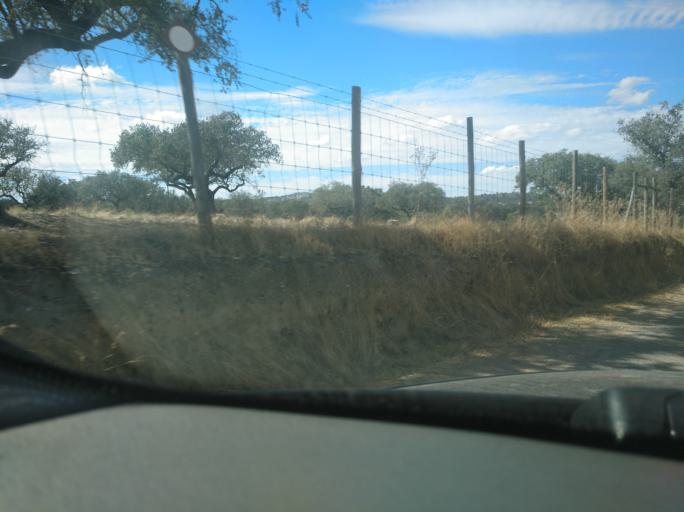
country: ES
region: Extremadura
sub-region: Provincia de Badajoz
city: La Codosera
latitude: 39.1320
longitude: -7.1566
